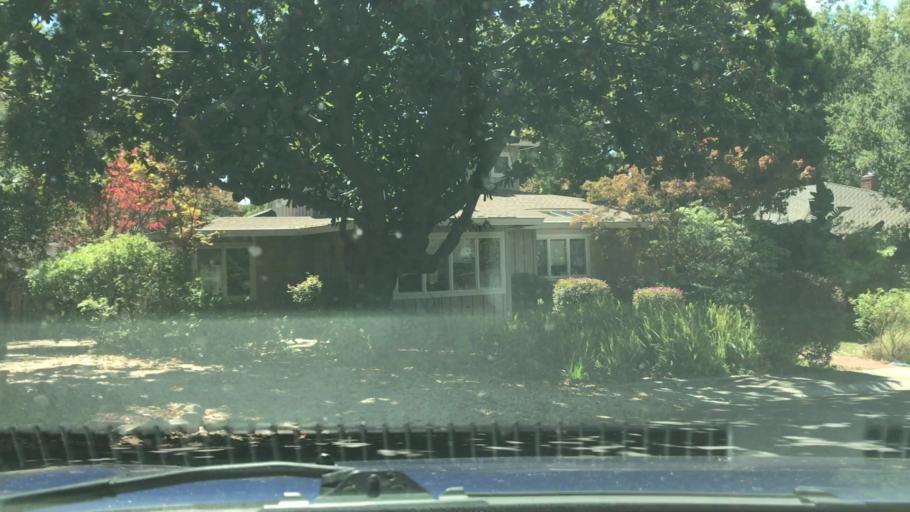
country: US
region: California
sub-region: San Mateo County
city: Menlo Park
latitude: 37.4548
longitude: -122.1609
